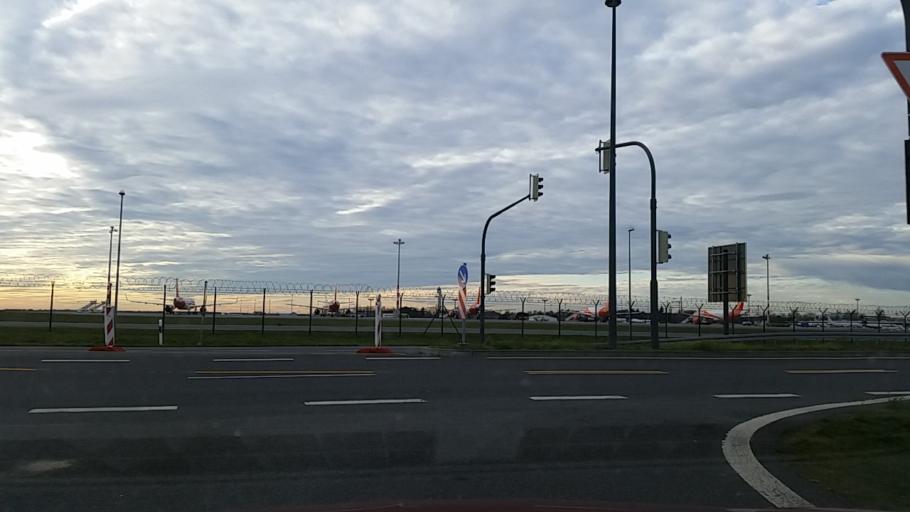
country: DE
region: Brandenburg
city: Schonefeld
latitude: 52.3852
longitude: 13.5285
